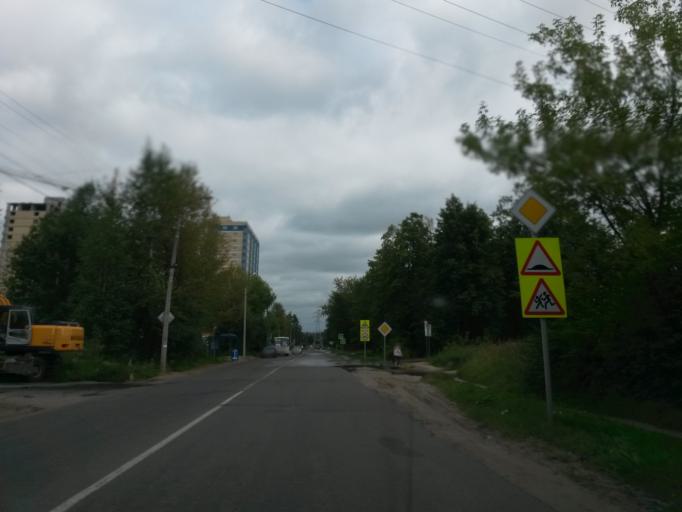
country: RU
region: Jaroslavl
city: Yaroslavl
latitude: 57.5830
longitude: 39.8728
